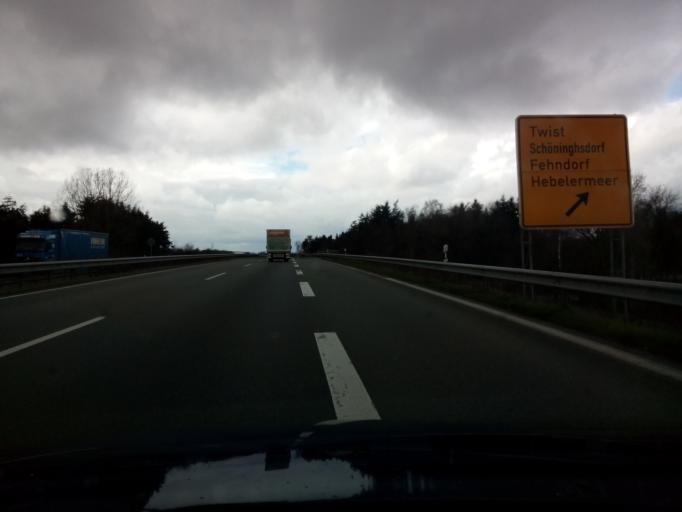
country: DE
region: Lower Saxony
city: Twist
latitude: 52.7225
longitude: 7.1022
